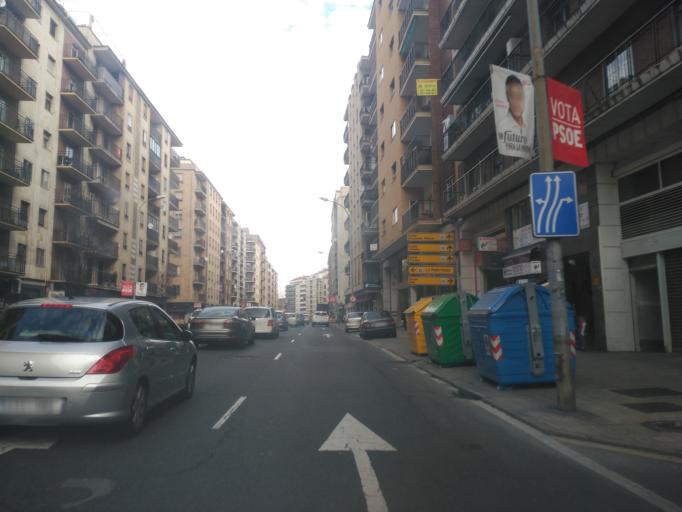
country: ES
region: Castille and Leon
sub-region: Provincia de Salamanca
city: Salamanca
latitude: 40.9635
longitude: -5.6584
